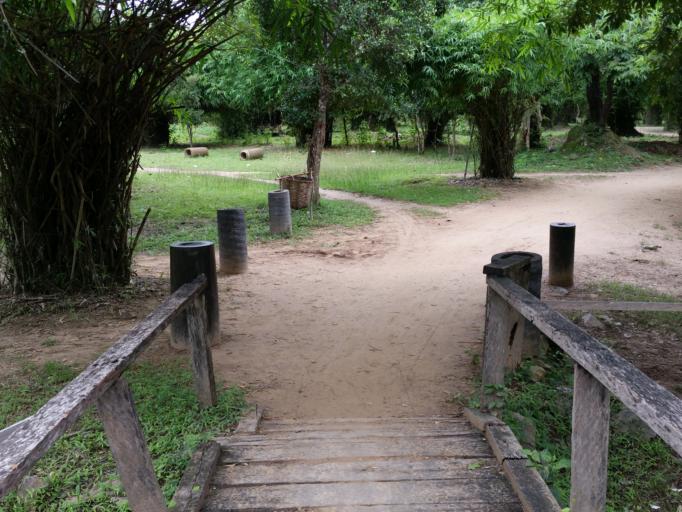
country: LA
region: Champasak
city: Khong
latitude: 13.9536
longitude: 105.9161
